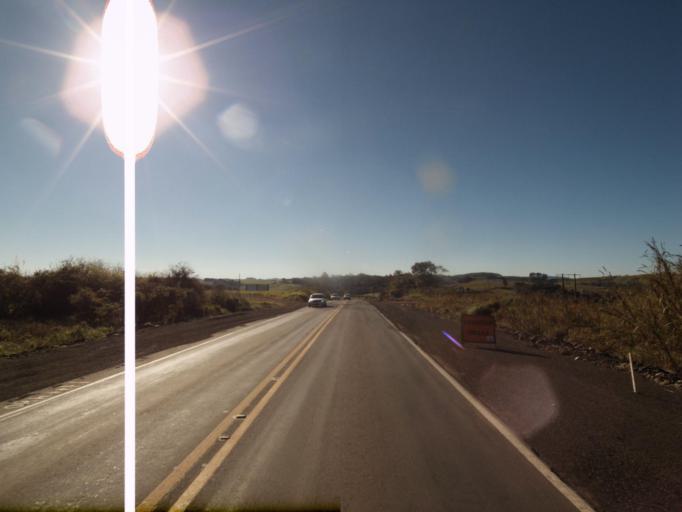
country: AR
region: Misiones
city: Bernardo de Irigoyen
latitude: -26.6497
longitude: -53.5187
